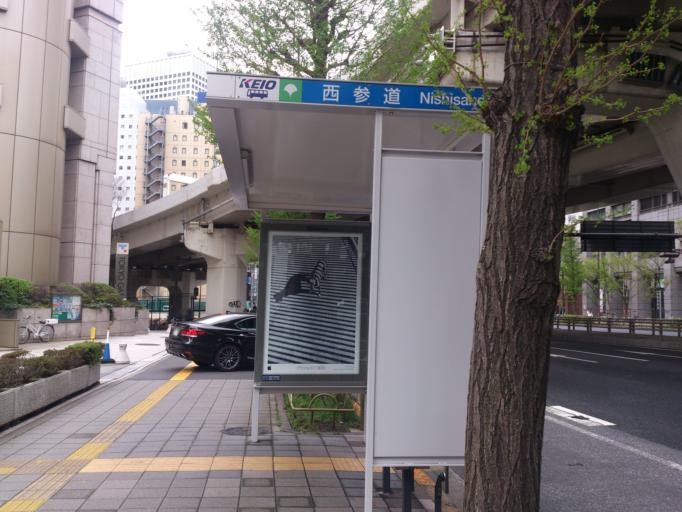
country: JP
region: Tokyo
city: Tokyo
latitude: 35.6848
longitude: 139.6914
